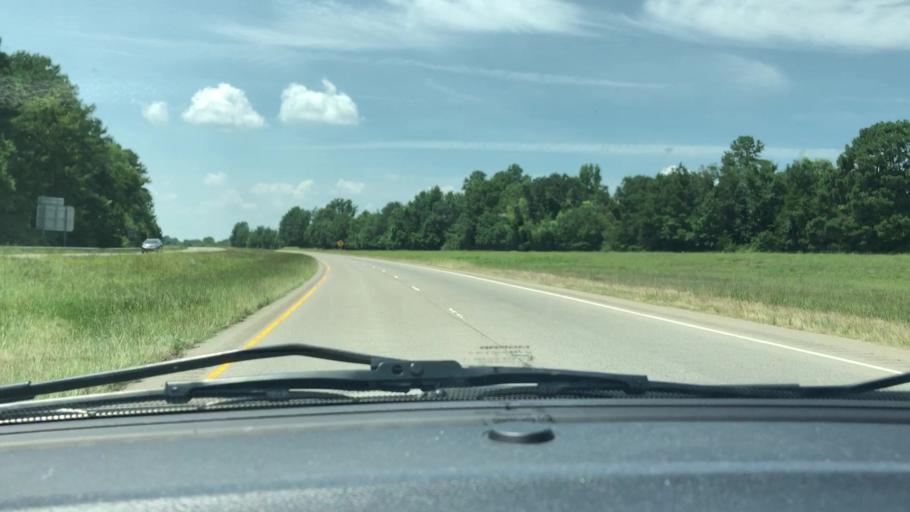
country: US
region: North Carolina
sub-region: Chatham County
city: Farmville
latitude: 35.6033
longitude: -79.3218
